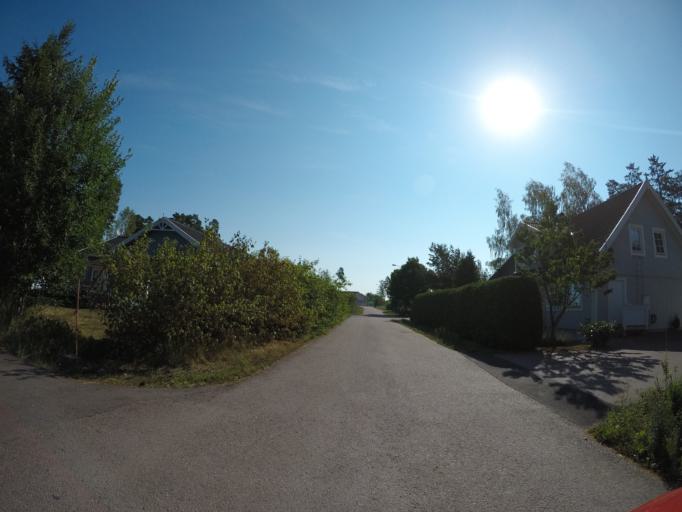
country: AX
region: Alands landsbygd
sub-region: Finstroem
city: Finstroem
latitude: 60.2288
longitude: 19.9777
